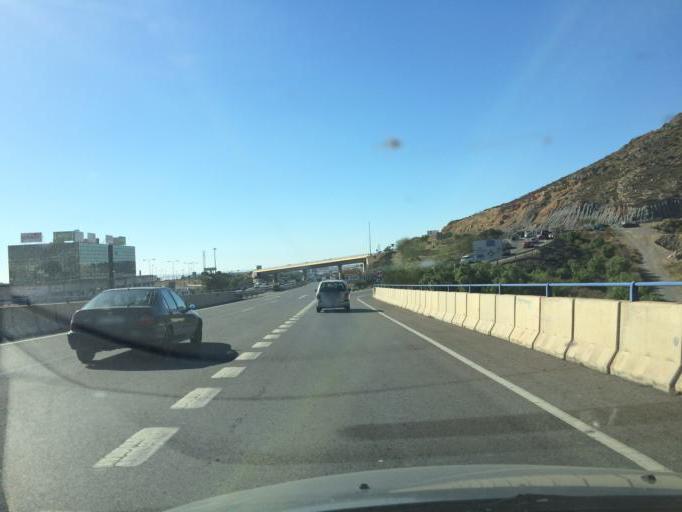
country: ES
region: Andalusia
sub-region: Provincia de Almeria
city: Aguadulce
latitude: 36.8224
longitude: -2.5959
